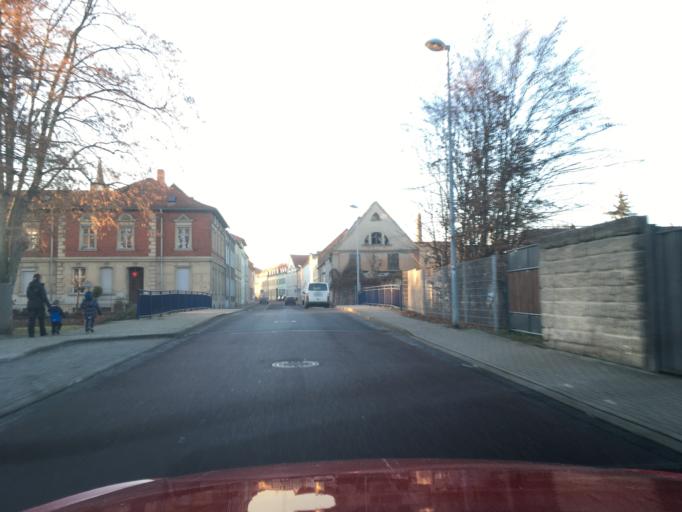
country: DE
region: Saxony-Anhalt
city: Rosslau
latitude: 51.8881
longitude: 12.2530
